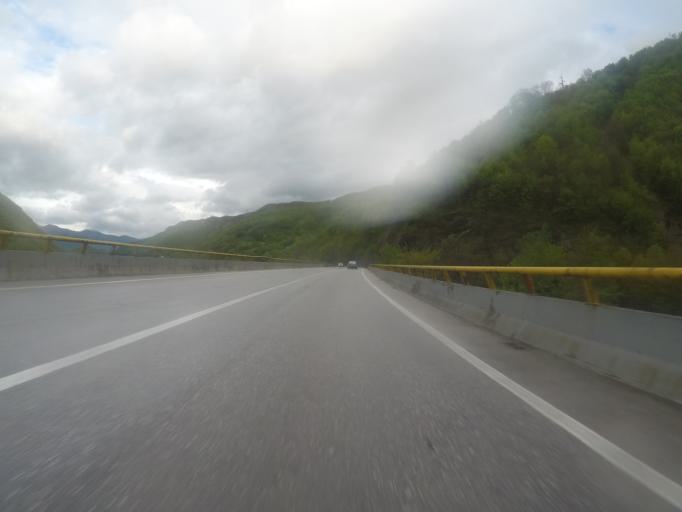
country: BA
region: Federation of Bosnia and Herzegovina
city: Jablanica
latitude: 43.6837
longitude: 17.7964
